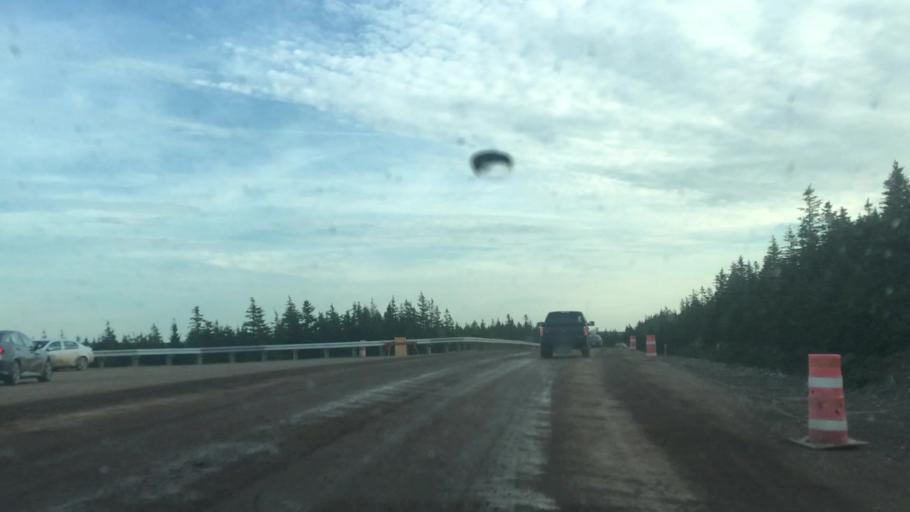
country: CA
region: Nova Scotia
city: Sydney Mines
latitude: 46.8035
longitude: -60.8436
